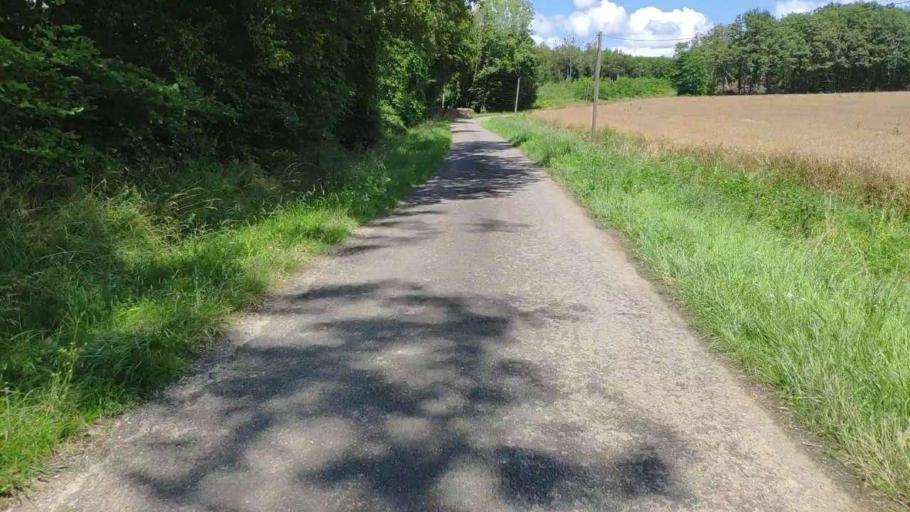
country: FR
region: Franche-Comte
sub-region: Departement du Jura
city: Chaussin
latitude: 46.8709
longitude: 5.4610
